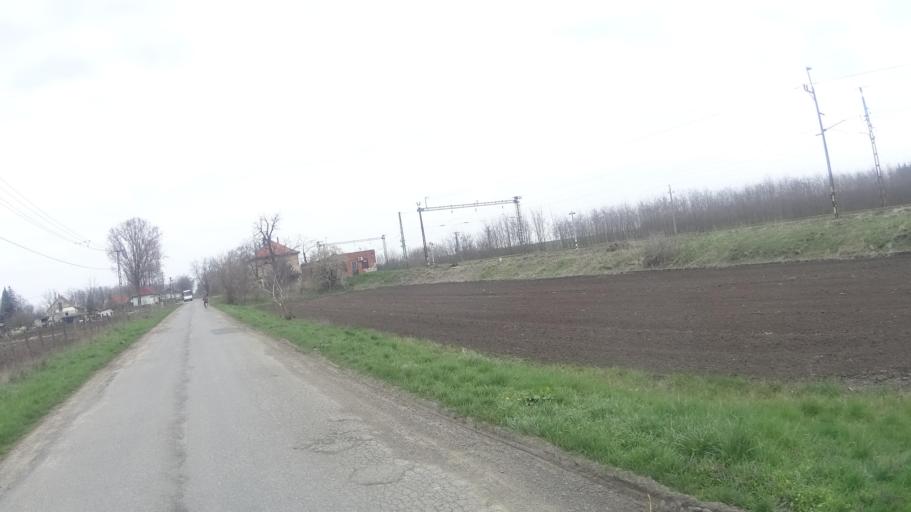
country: HU
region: Fejer
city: Sarosd
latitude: 46.9780
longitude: 18.6347
